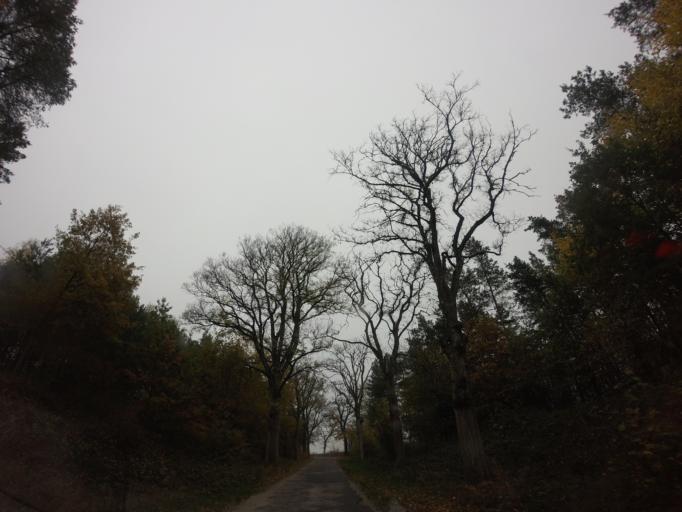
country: PL
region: West Pomeranian Voivodeship
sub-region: Powiat choszczenski
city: Krzecin
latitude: 53.0313
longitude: 15.5374
